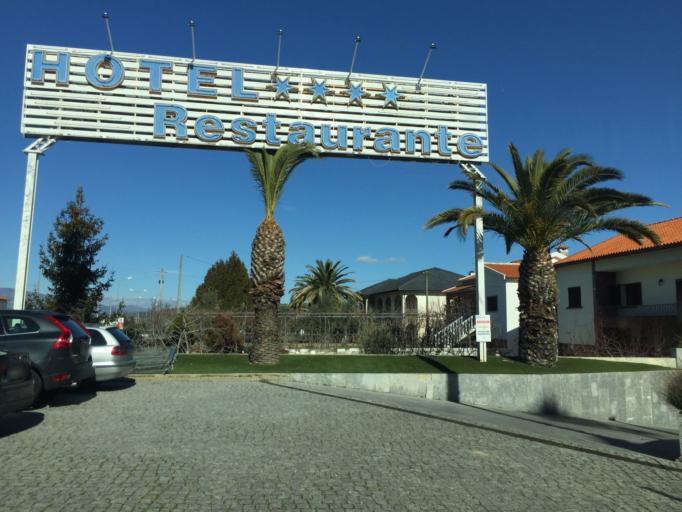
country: PT
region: Castelo Branco
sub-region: Concelho do Fundao
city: Fundao
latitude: 40.1666
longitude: -7.4957
